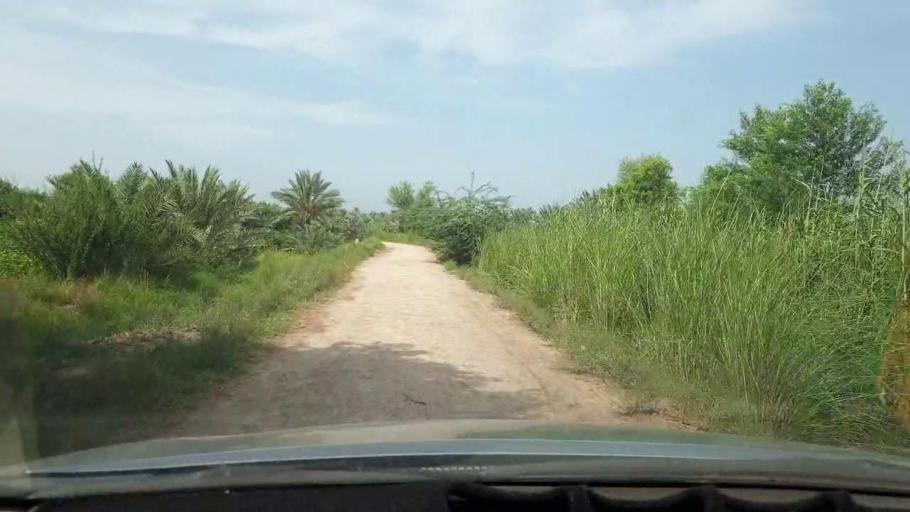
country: PK
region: Sindh
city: Khairpur
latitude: 27.4818
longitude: 68.7464
